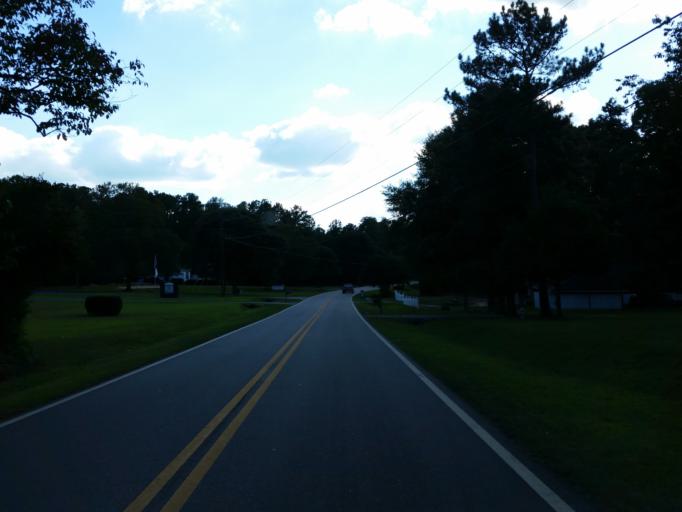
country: US
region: Georgia
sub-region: Butts County
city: Indian Springs
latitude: 33.1839
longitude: -84.0110
